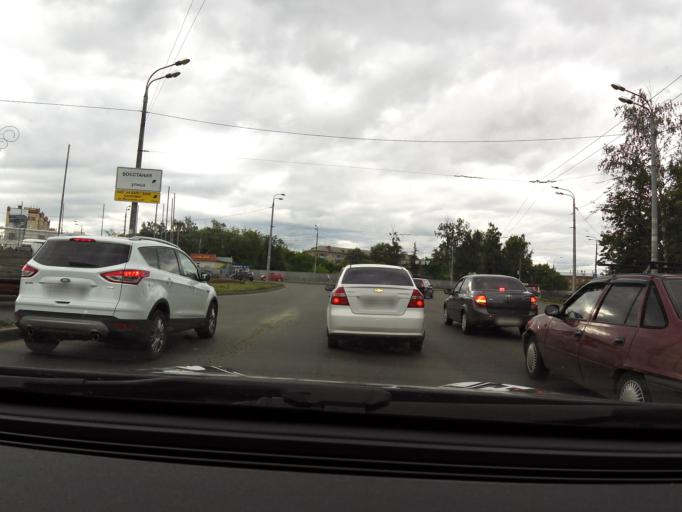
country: RU
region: Tatarstan
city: Staroye Arakchino
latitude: 55.8249
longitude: 49.0435
